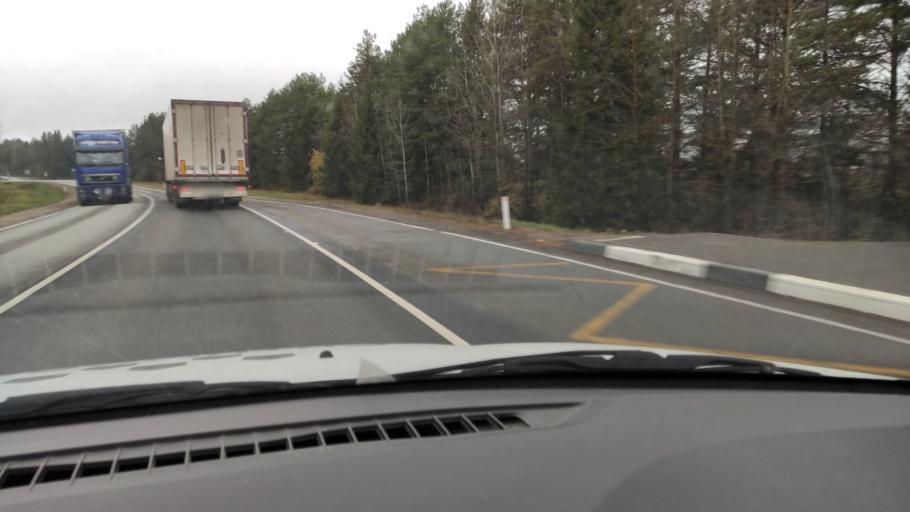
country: RU
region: Kirov
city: Slobodskoy
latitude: 58.7558
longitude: 50.3253
